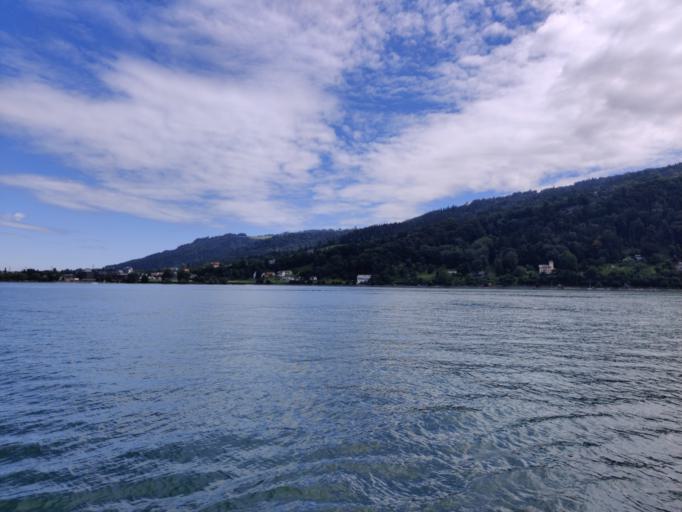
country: AT
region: Vorarlberg
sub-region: Politischer Bezirk Bregenz
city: Bregenz
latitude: 47.5149
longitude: 9.7432
